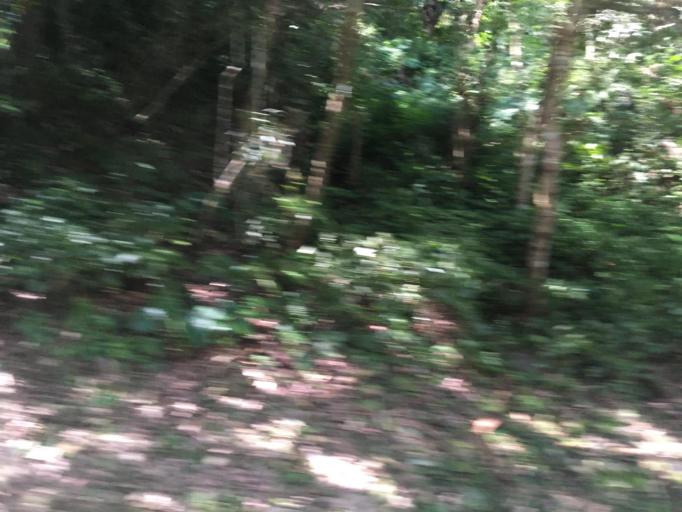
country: TW
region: Taiwan
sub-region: Yilan
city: Yilan
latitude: 24.7549
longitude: 121.6126
